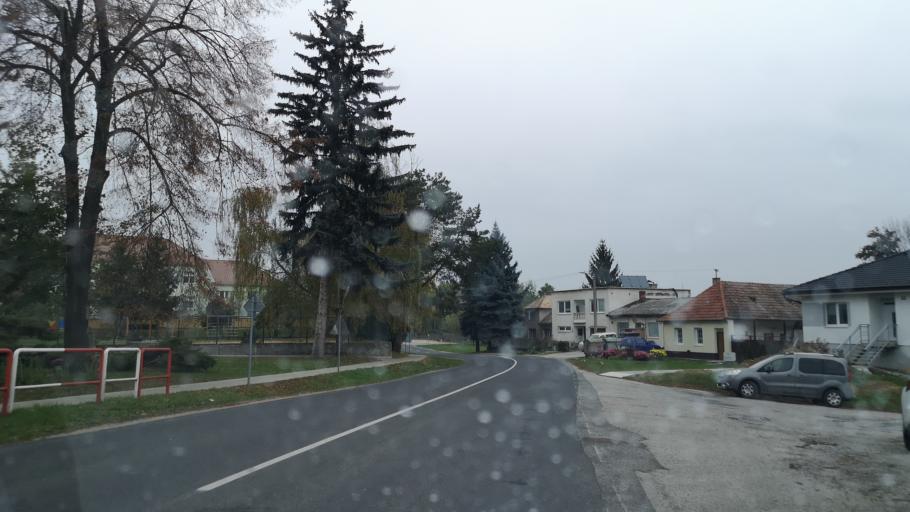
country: SK
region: Trnavsky
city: Vrbove
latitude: 48.5248
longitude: 17.6100
